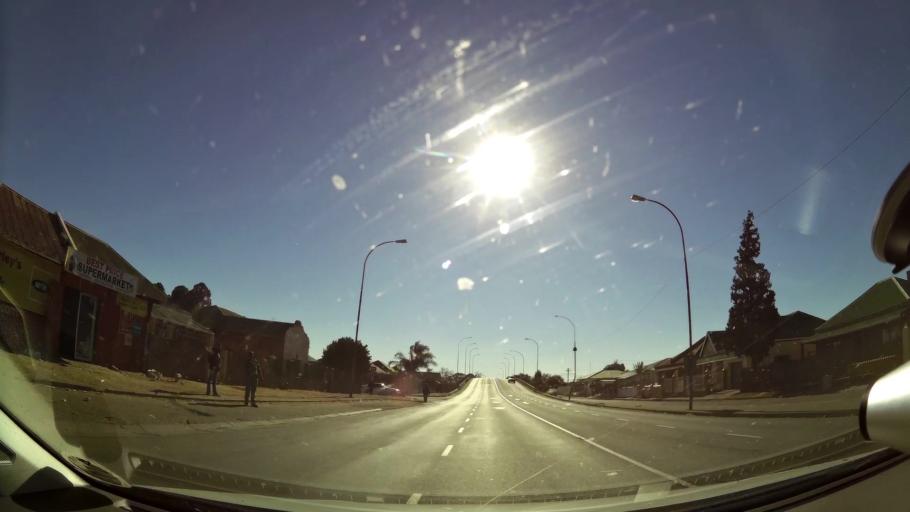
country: ZA
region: Northern Cape
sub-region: Frances Baard District Municipality
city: Kimberley
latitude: -28.7263
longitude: 24.7681
